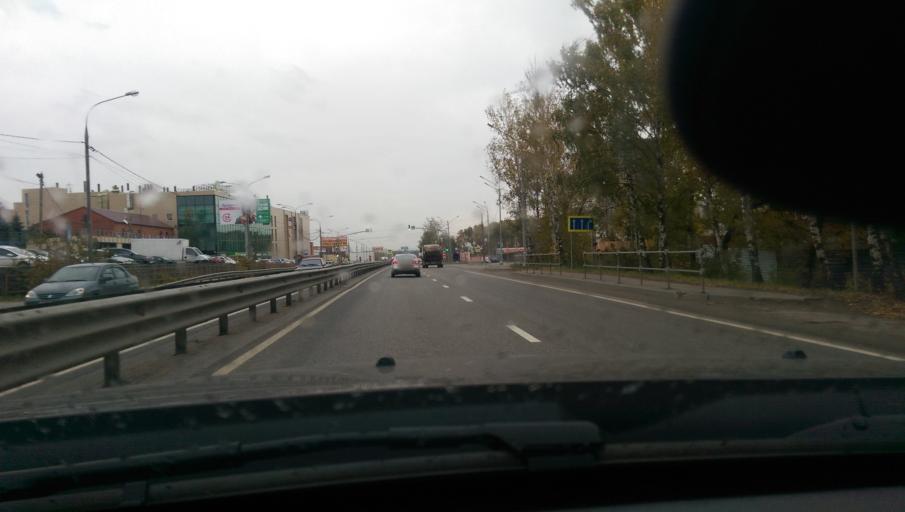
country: RU
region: Moscow
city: Vatutino
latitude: 55.9228
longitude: 37.6631
